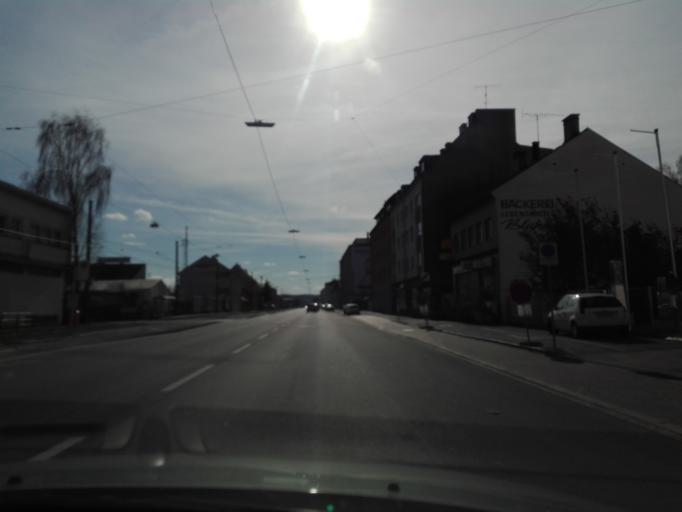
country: AT
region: Upper Austria
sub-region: Linz Stadt
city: Linz
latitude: 48.2690
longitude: 14.3160
